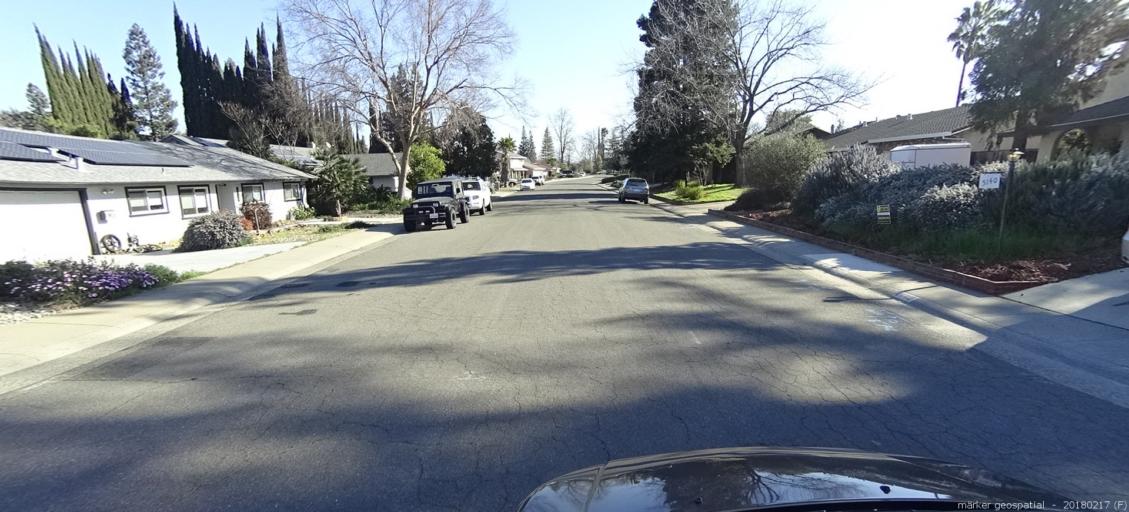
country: US
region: California
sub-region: Sacramento County
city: Folsom
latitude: 38.6587
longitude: -121.1984
